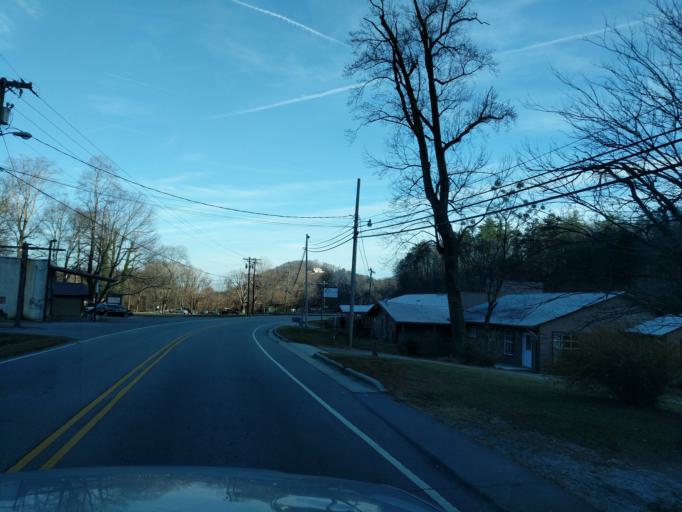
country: US
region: North Carolina
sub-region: Rutherford County
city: Lake Lure
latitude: 35.4368
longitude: -82.2370
